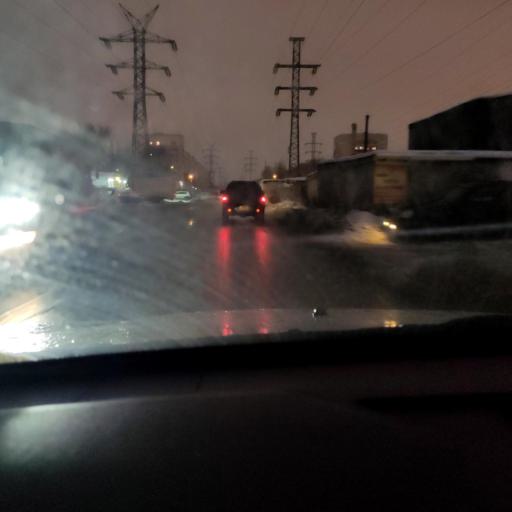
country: RU
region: Samara
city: Petra-Dubrava
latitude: 53.2413
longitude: 50.2901
